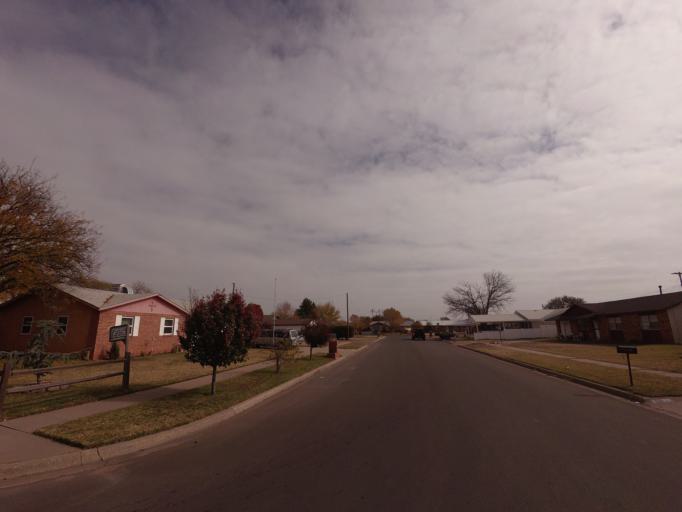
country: US
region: New Mexico
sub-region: Curry County
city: Clovis
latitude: 34.4299
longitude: -103.2177
